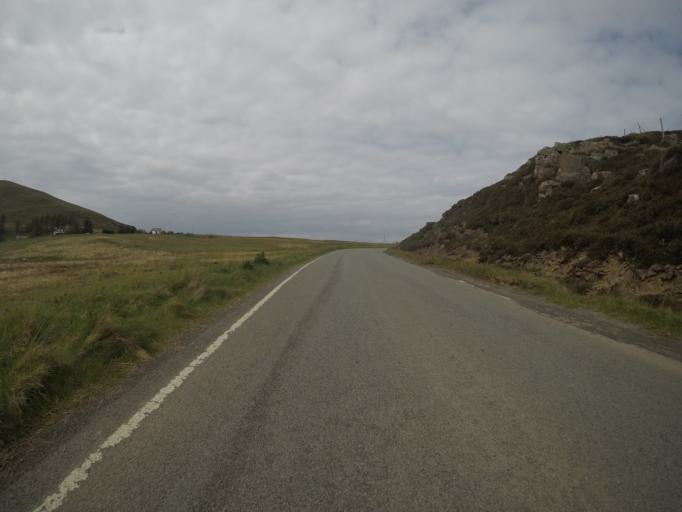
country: GB
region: Scotland
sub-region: Highland
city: Portree
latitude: 57.6828
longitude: -6.3247
